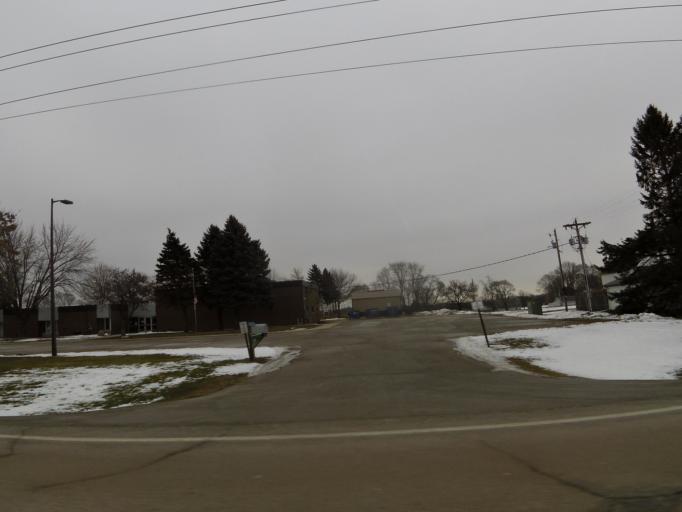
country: US
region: Minnesota
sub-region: Carver County
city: Carver
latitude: 44.7198
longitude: -93.6843
